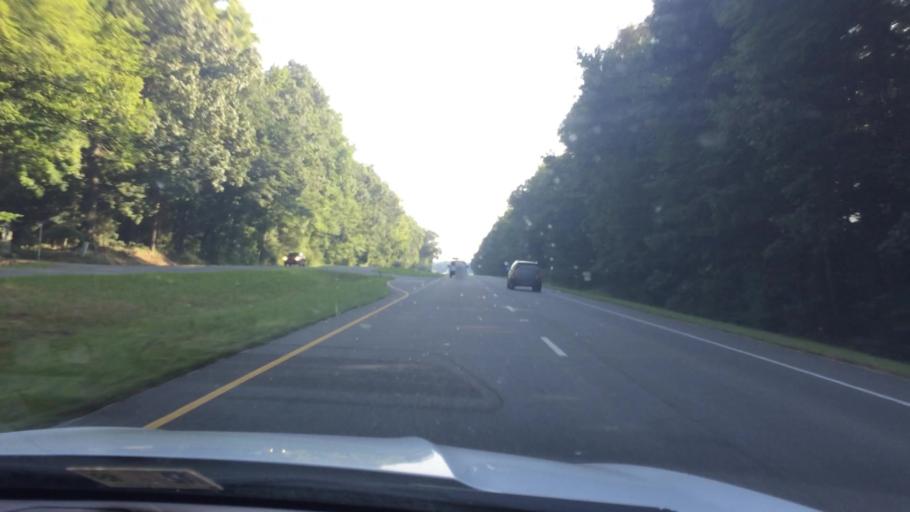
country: US
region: Virginia
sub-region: Gloucester County
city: Gloucester Courthouse
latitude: 37.4315
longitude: -76.4808
